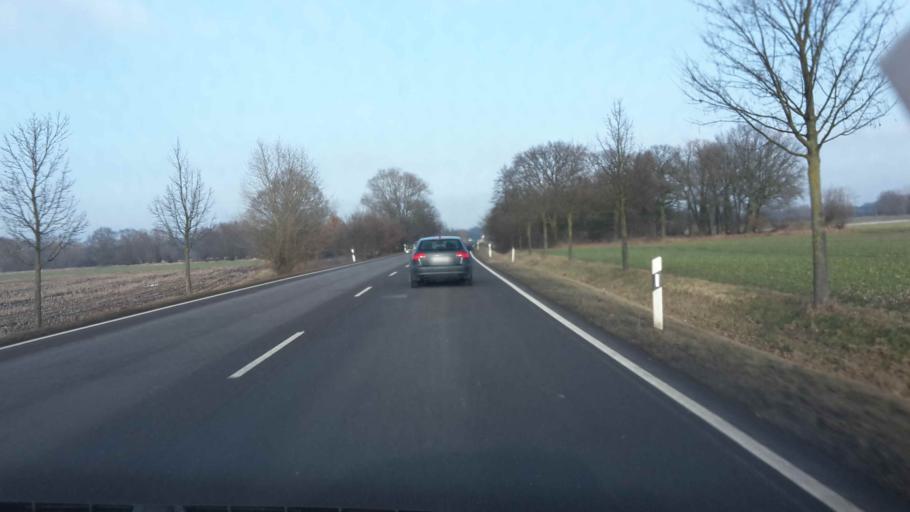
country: DE
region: Brandenburg
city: Wittenberge
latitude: 52.9598
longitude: 11.7276
